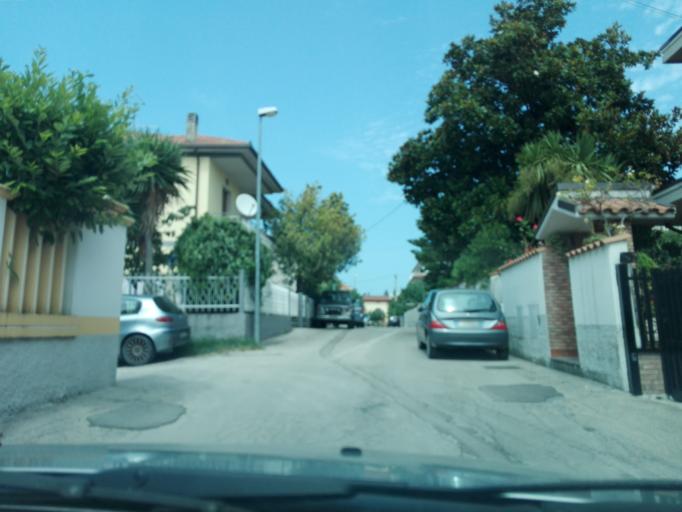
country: IT
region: Abruzzo
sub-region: Provincia di Pescara
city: Montesilvano Marina
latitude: 42.5076
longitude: 14.1390
